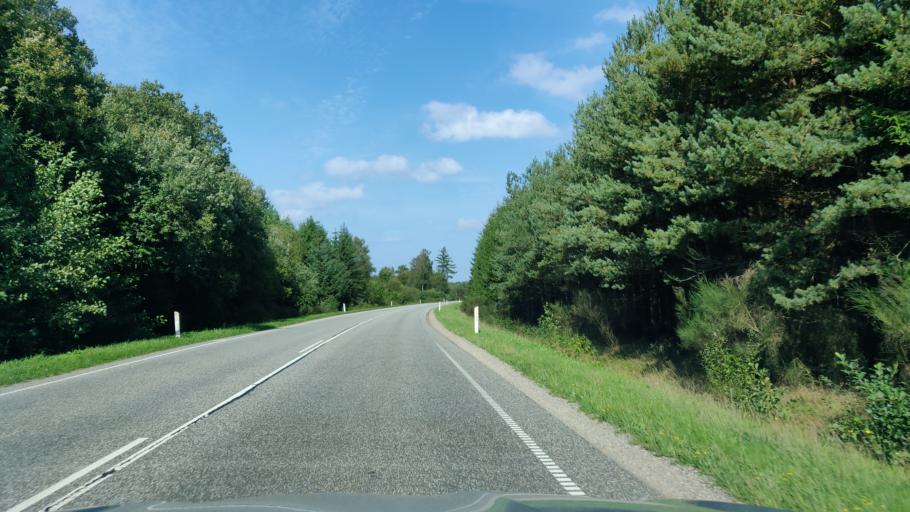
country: DK
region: Central Jutland
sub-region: Herning Kommune
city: Sunds
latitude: 56.3517
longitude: 8.9733
